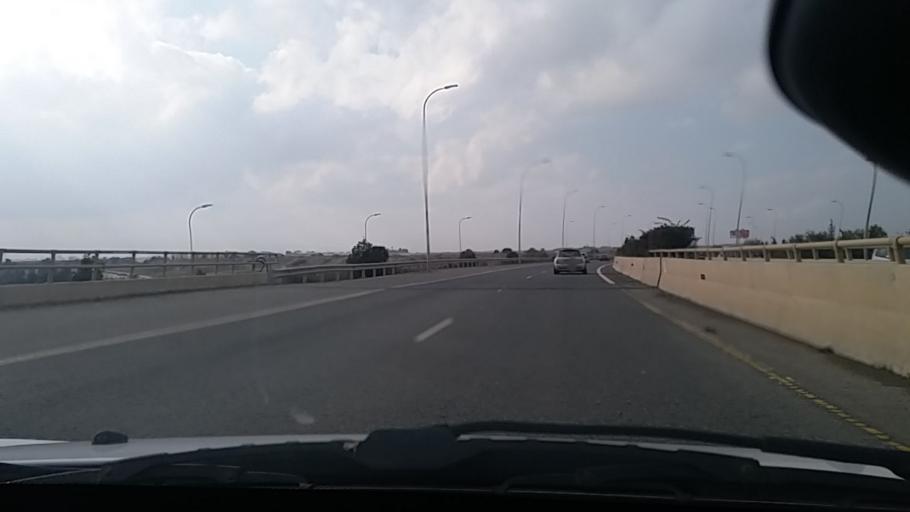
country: CY
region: Lefkosia
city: Kato Deftera
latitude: 35.1290
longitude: 33.2965
